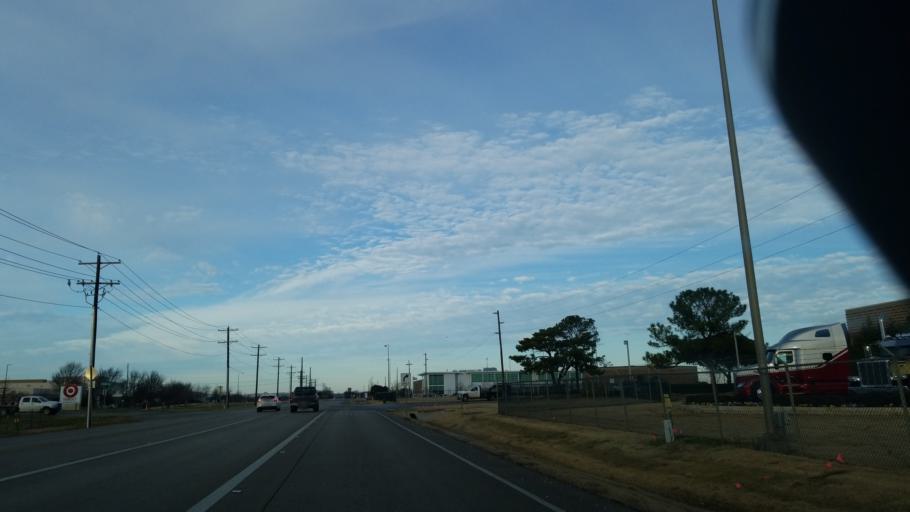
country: US
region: Texas
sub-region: Denton County
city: Denton
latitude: 33.2017
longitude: -97.1766
